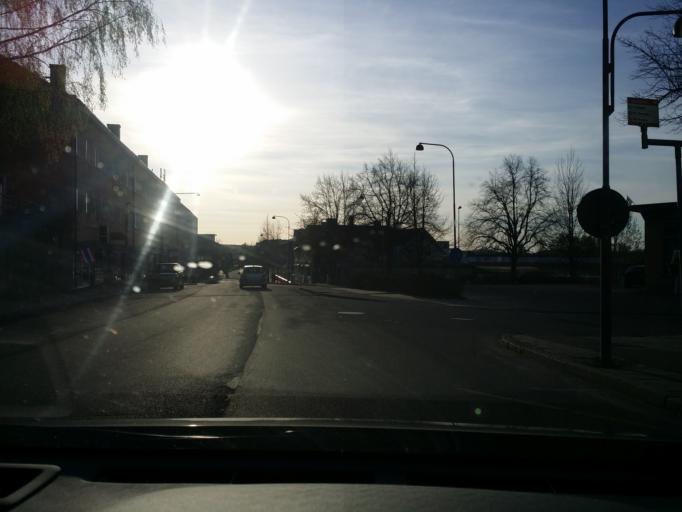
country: SE
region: Dalarna
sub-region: Avesta Kommun
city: Avesta
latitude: 60.1447
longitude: 16.1761
